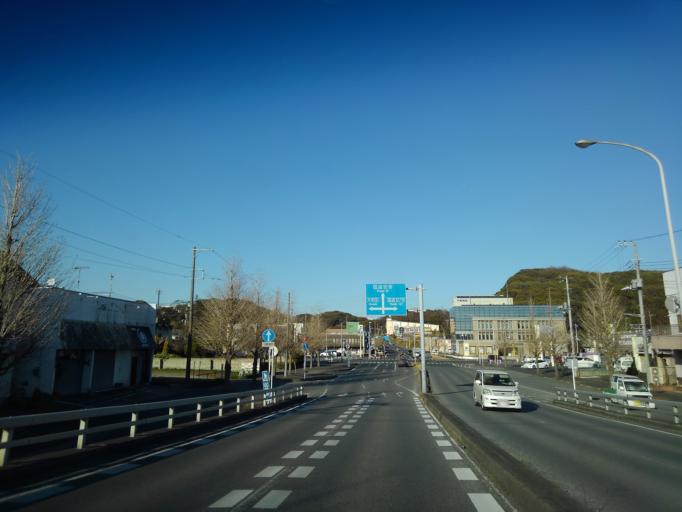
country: JP
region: Chiba
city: Kimitsu
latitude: 35.3363
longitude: 139.8904
